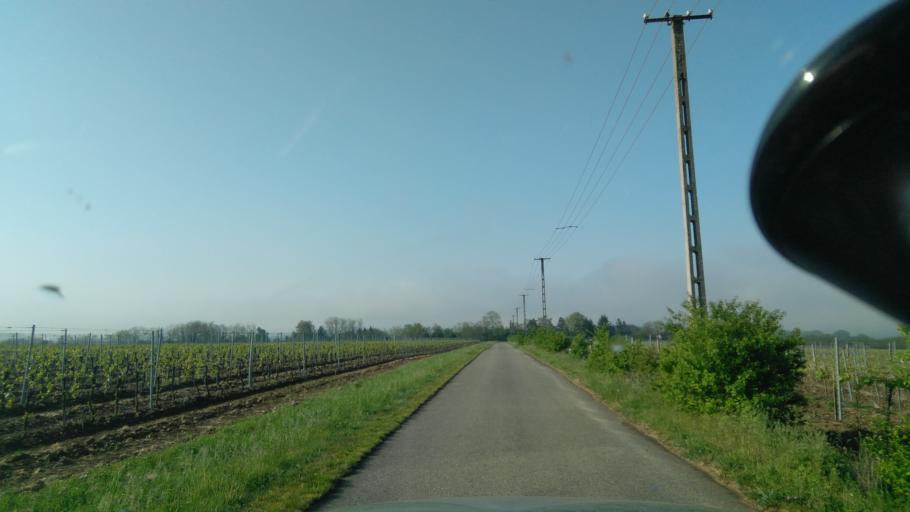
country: HU
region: Zala
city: Sarmellek
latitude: 46.7495
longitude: 17.1404
